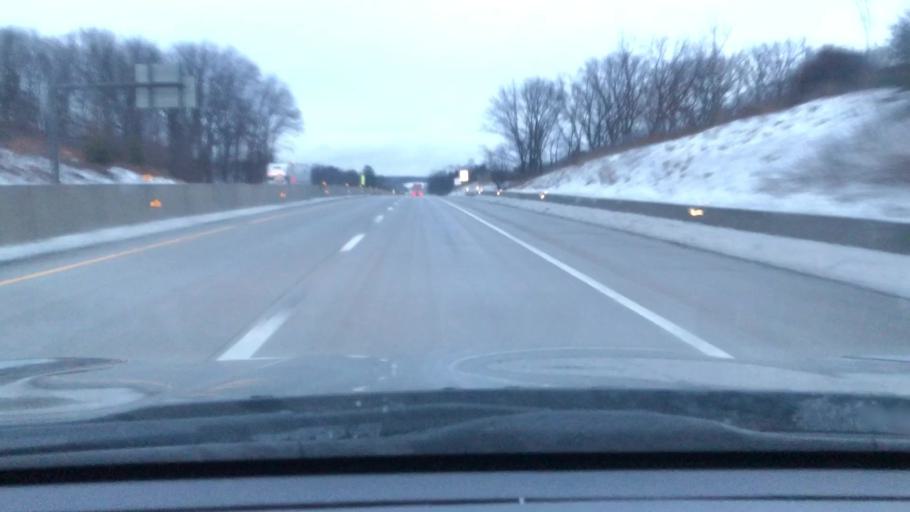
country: US
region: Pennsylvania
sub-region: Berks County
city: Hamburg
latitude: 40.5662
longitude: -75.9730
